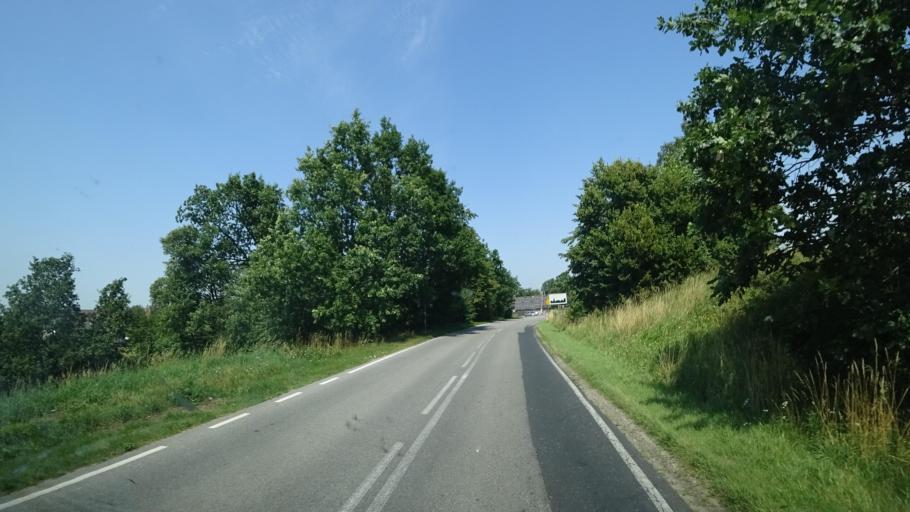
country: PL
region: Pomeranian Voivodeship
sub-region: Powiat koscierski
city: Dziemiany
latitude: 53.9563
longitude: 17.7448
